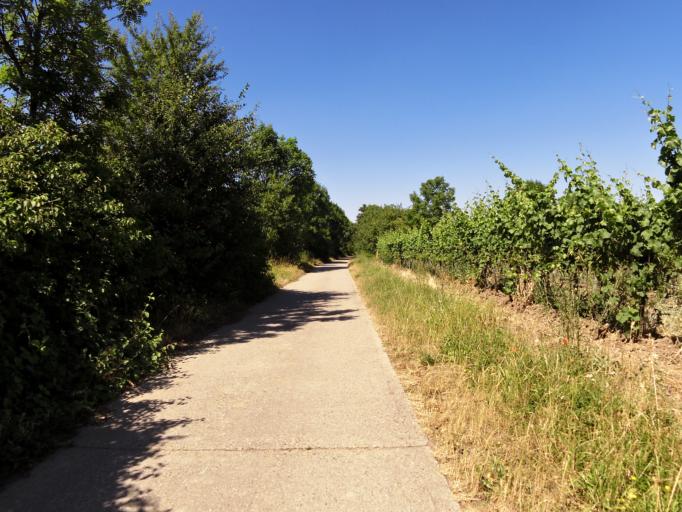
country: DE
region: Rheinland-Pfalz
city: Deidesheim
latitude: 49.3821
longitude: 8.1753
